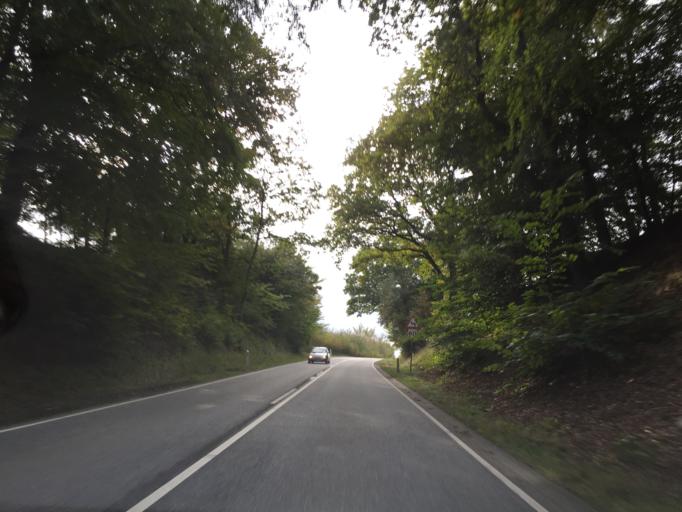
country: DK
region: Central Jutland
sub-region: Randers Kommune
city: Langa
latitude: 56.3505
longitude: 9.8944
